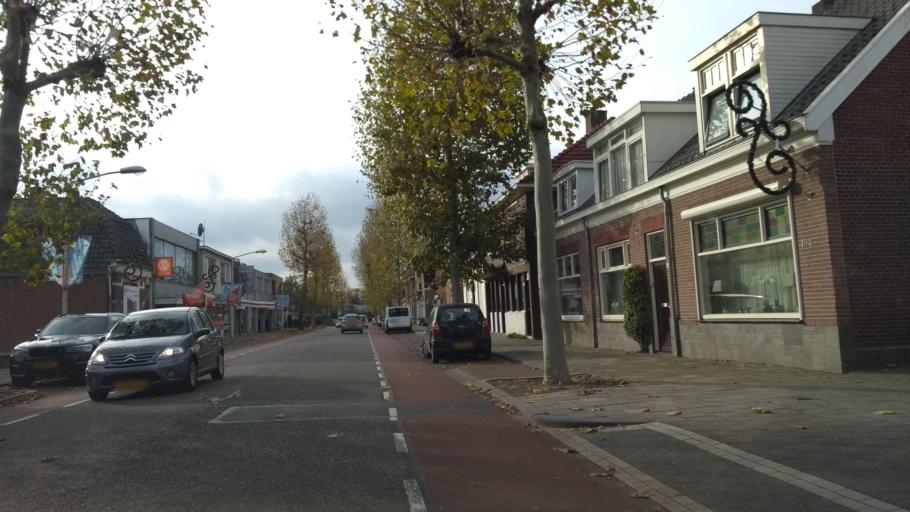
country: NL
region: Overijssel
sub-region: Gemeente Almelo
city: Almelo
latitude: 52.3661
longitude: 6.6754
